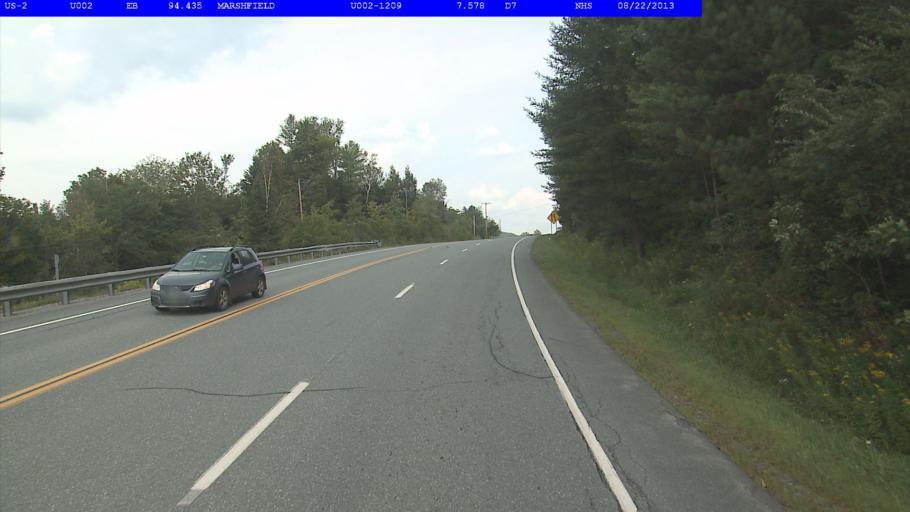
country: US
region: Vermont
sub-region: Caledonia County
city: Hardwick
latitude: 44.3573
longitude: -72.3347
